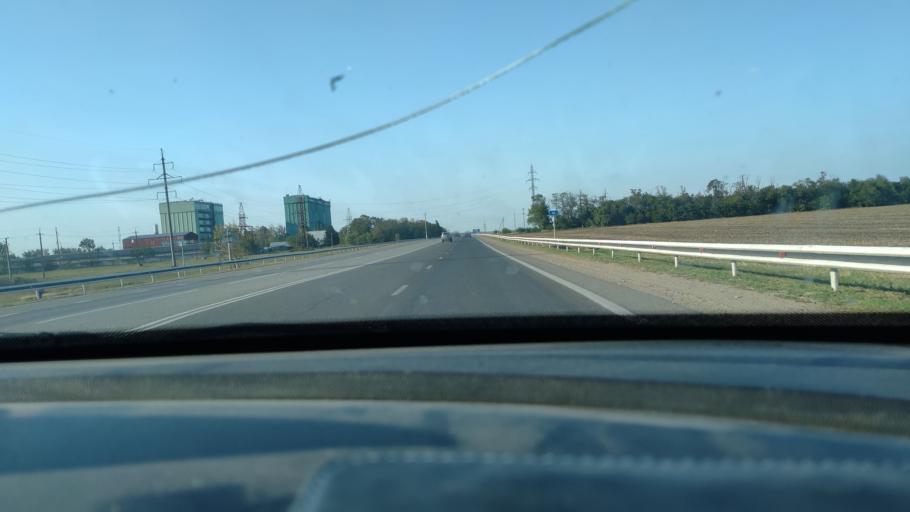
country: RU
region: Krasnodarskiy
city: Timashevsk
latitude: 45.6143
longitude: 38.9872
